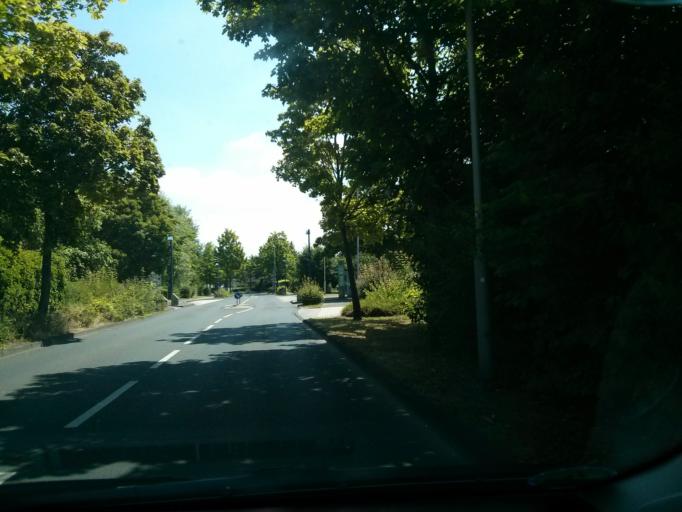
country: DE
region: North Rhine-Westphalia
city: Meckenheim
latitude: 50.6240
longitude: 7.0463
